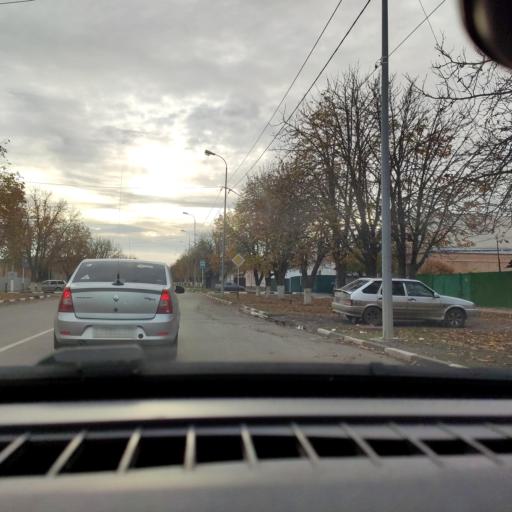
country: RU
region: Belgorod
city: Alekseyevka
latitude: 50.6335
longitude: 38.6800
